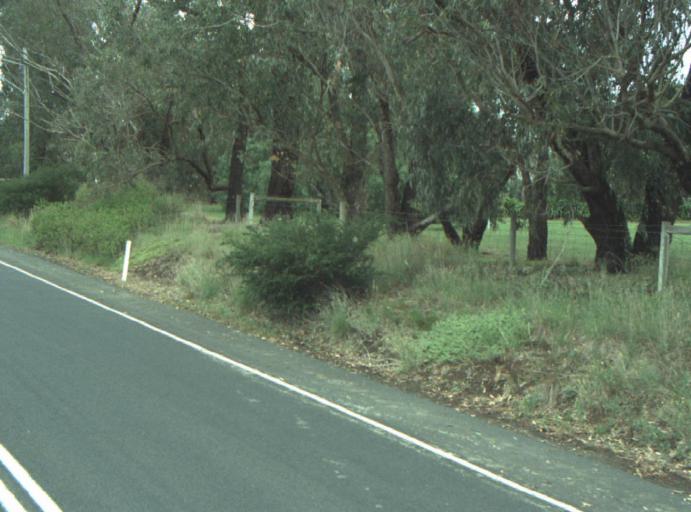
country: AU
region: Victoria
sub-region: Greater Geelong
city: Leopold
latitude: -38.2102
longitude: 144.5093
